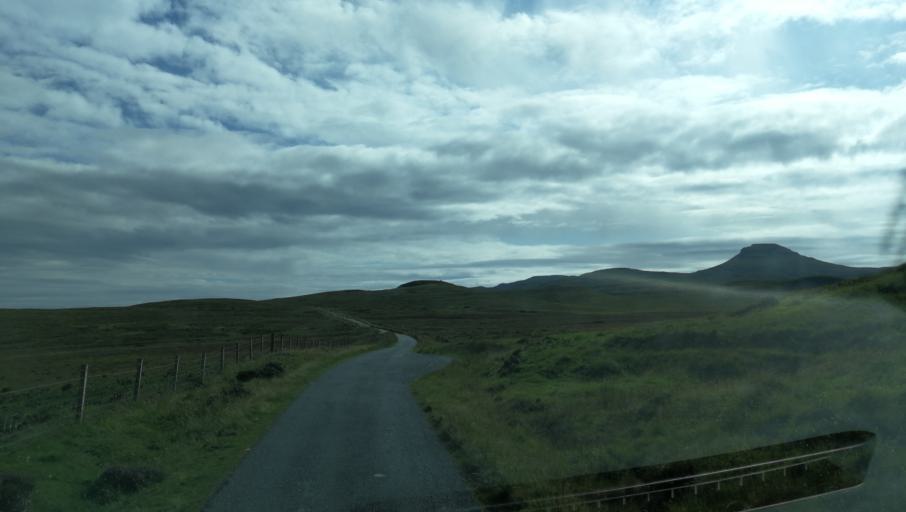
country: GB
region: Scotland
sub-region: Highland
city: Isle of Skye
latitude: 57.4178
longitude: -6.5654
